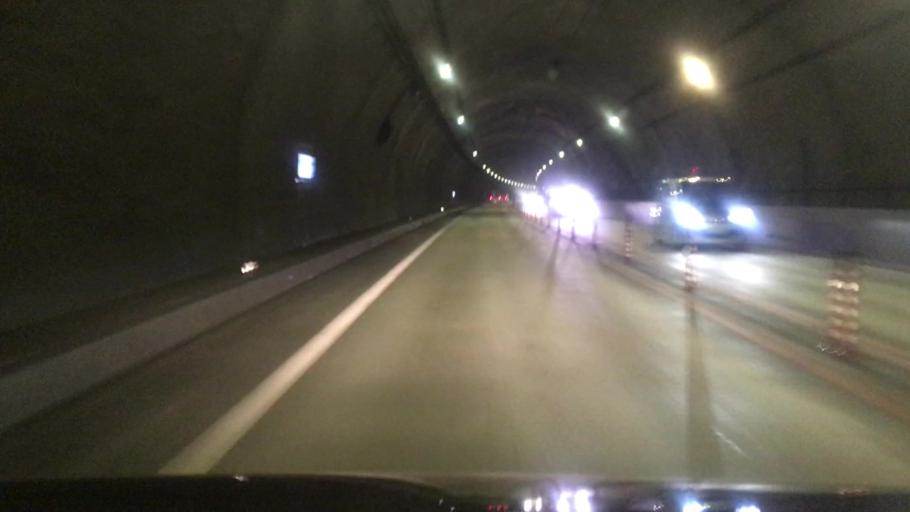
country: JP
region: Hyogo
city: Toyooka
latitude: 35.3670
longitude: 134.7579
